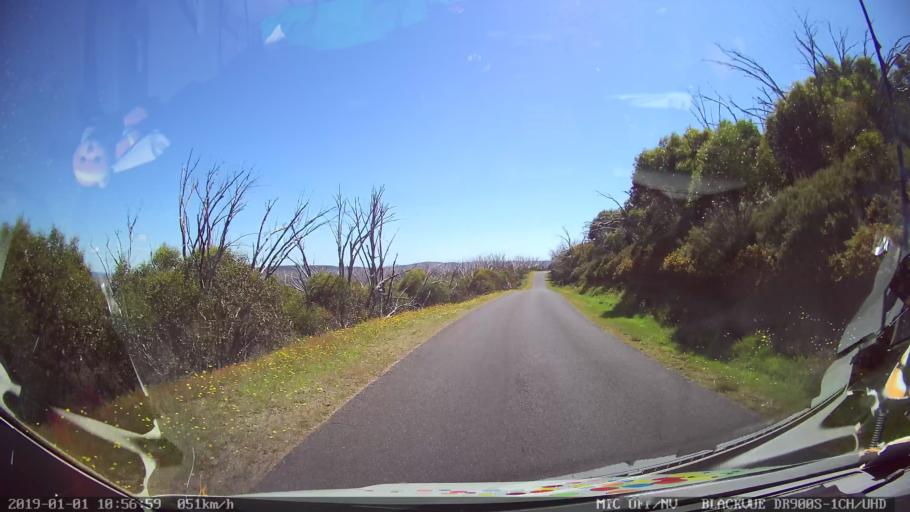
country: AU
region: New South Wales
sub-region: Snowy River
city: Jindabyne
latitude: -36.0005
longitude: 148.3940
